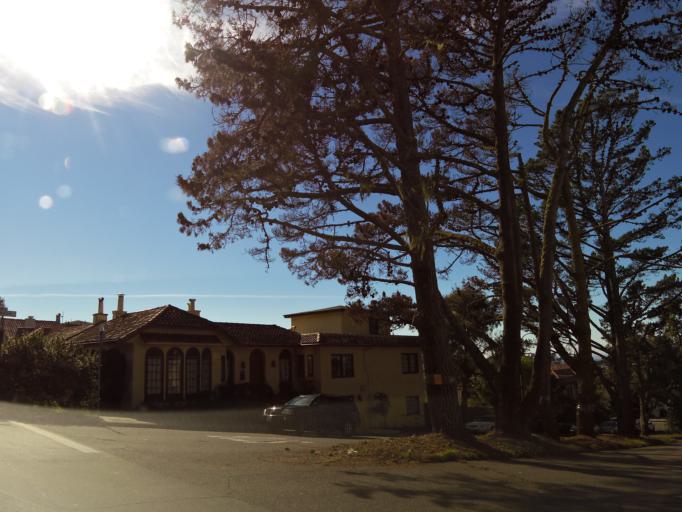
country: US
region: California
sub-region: San Mateo County
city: Daly City
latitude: 37.7544
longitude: -122.4733
